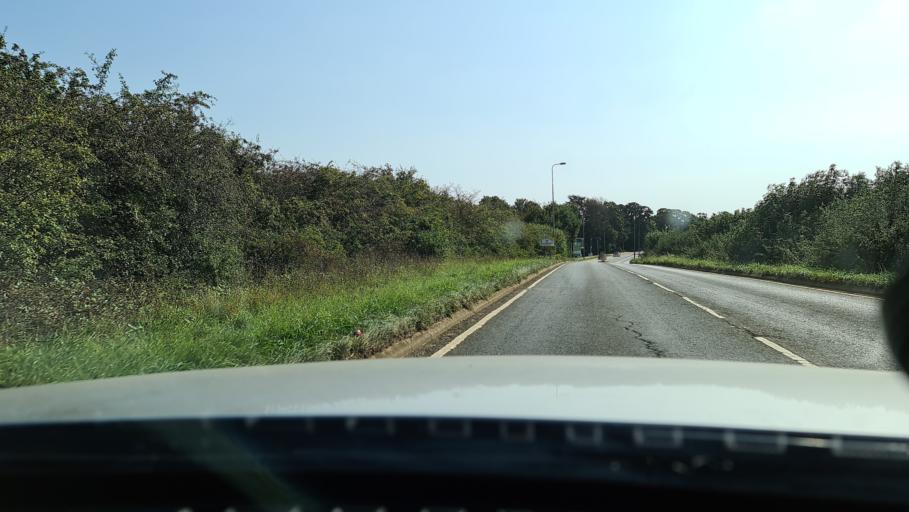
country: GB
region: England
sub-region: Oxfordshire
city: Hanwell
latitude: 52.0821
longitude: -1.3701
